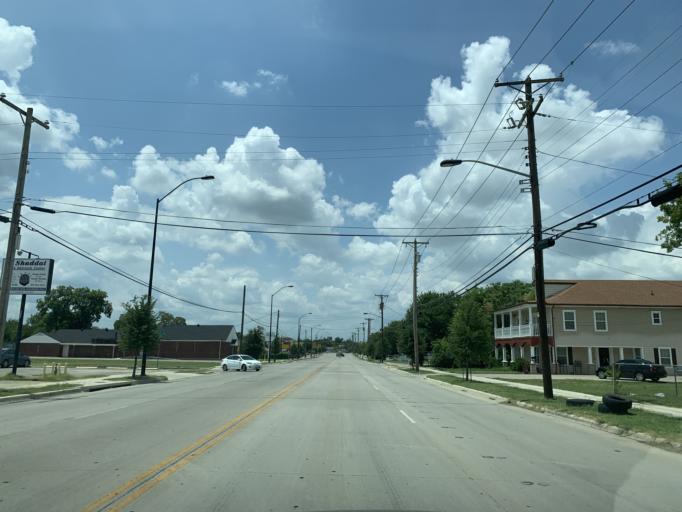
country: US
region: Texas
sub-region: Tarrant County
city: Fort Worth
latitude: 32.7313
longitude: -97.2658
